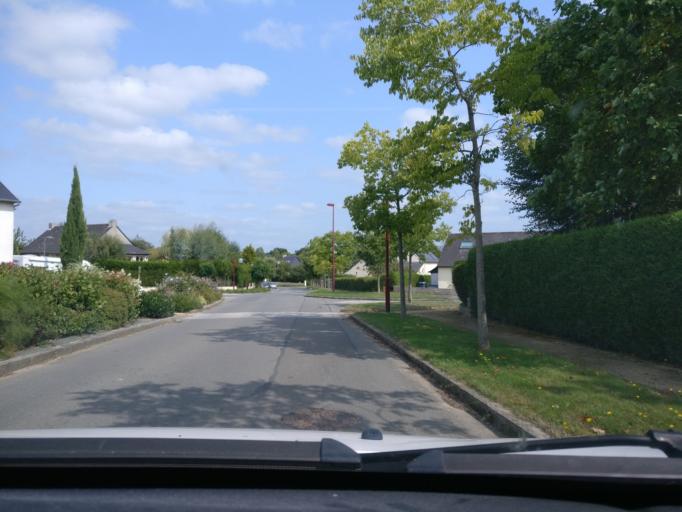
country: FR
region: Brittany
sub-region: Departement d'Ille-et-Vilaine
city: Chasne-sur-Illet
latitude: 48.2401
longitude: -1.5637
